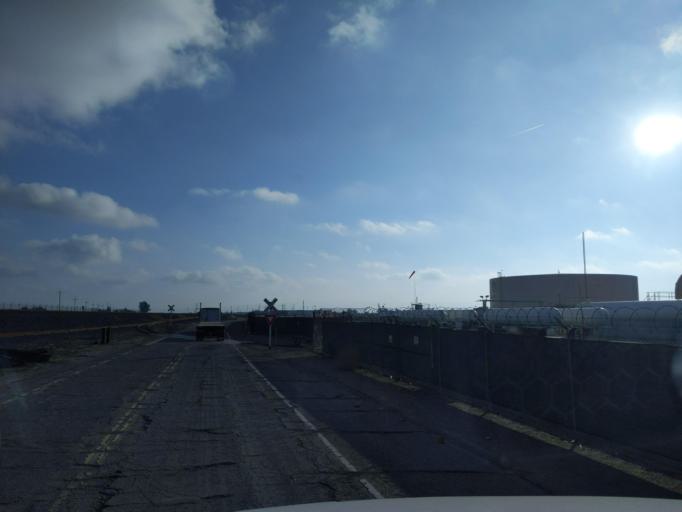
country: US
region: California
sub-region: San Joaquin County
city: Lathrop
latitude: 37.8062
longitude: -121.2756
